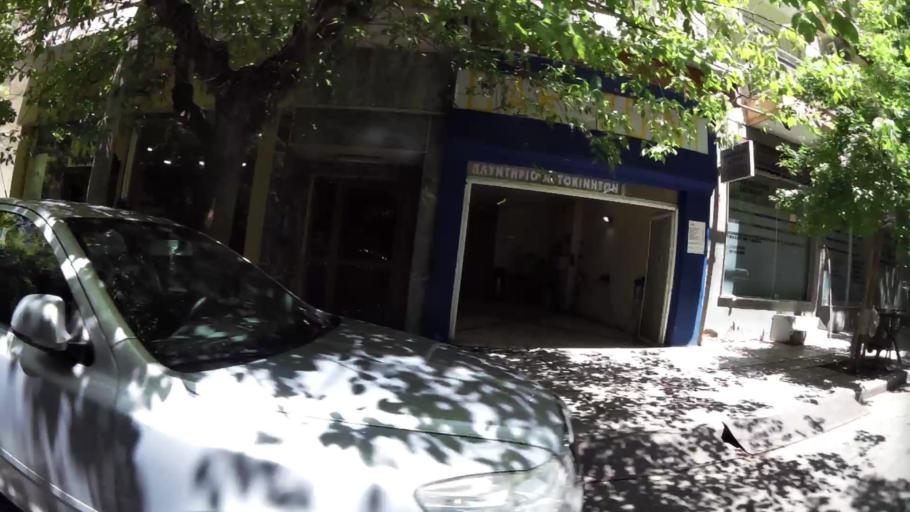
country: GR
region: Central Macedonia
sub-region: Nomos Thessalonikis
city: Triandria
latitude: 40.6156
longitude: 22.9550
